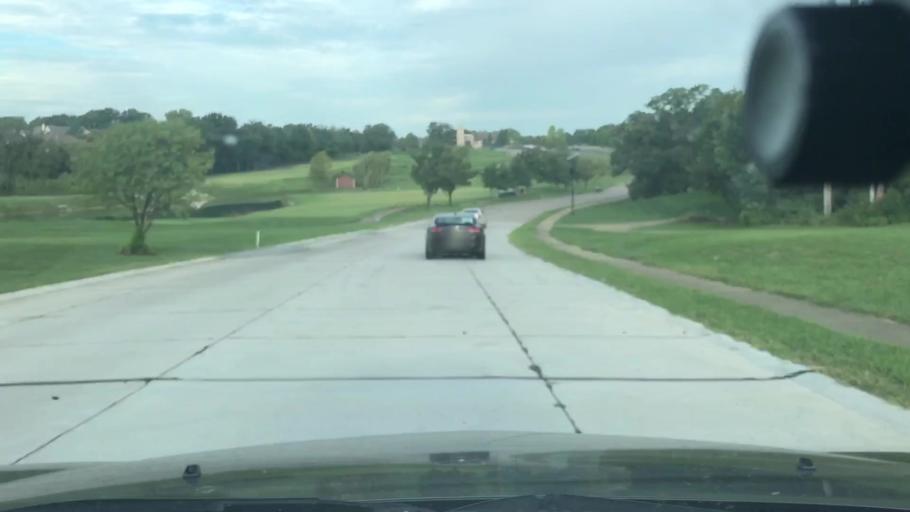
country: US
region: Missouri
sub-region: Saint Charles County
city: Wentzville
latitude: 38.8175
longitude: -90.8915
